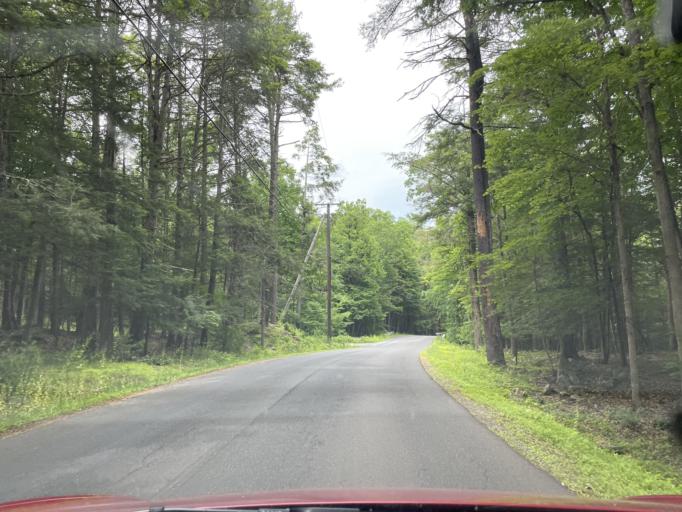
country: US
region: New York
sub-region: Ulster County
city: Zena
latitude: 41.9983
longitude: -74.0560
